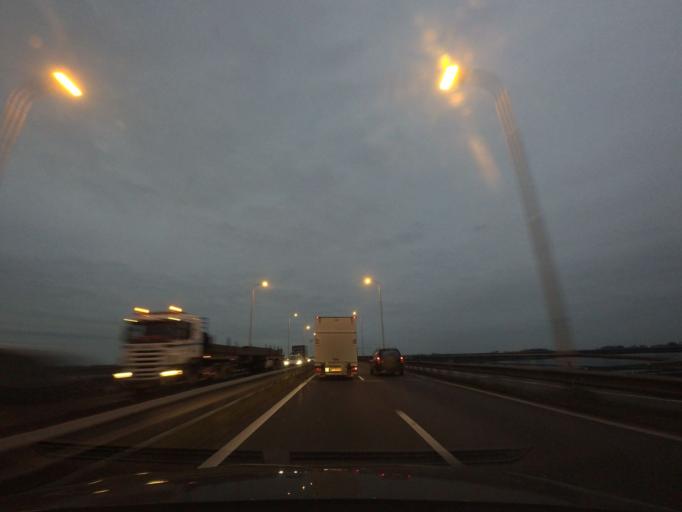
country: NL
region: South Holland
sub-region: Gemeente Gorinchem
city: Gorinchem
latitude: 51.8309
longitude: 4.9437
